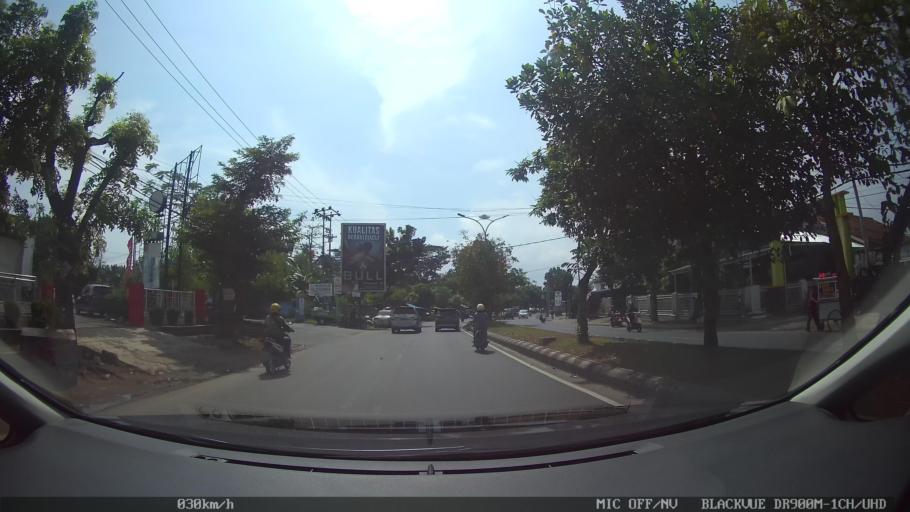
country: ID
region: Lampung
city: Kedaton
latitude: -5.3788
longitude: 105.2622
